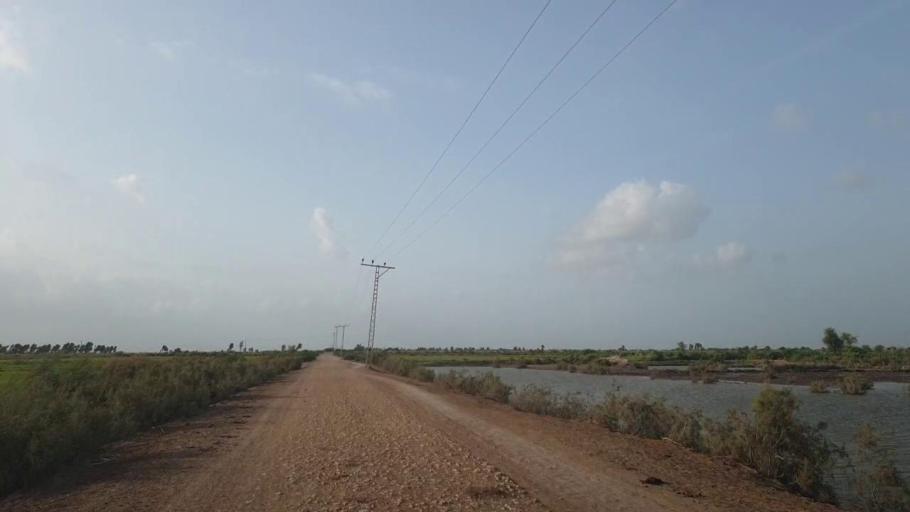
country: PK
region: Sindh
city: Tando Bago
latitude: 24.6527
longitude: 69.1119
